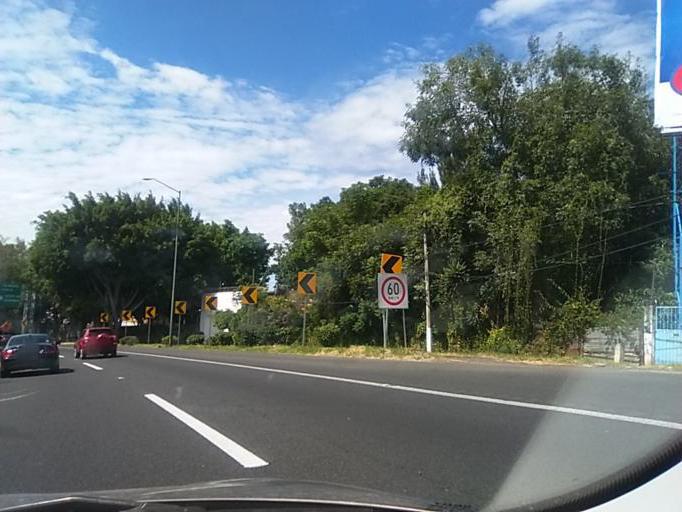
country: MX
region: Morelos
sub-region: Cuernavaca
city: Fraccionamiento Lomas de Ahuatlan
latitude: 18.9738
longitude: -99.2390
